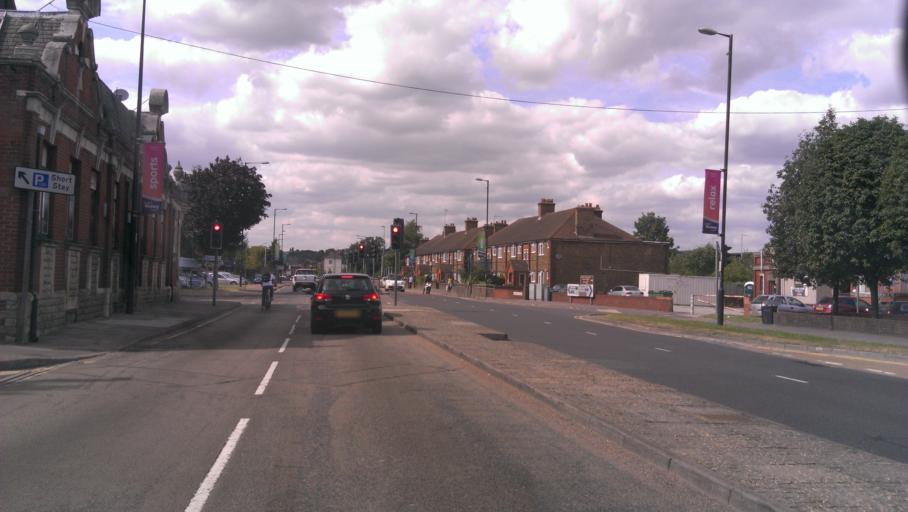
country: GB
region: England
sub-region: Medway
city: Rochester
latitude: 51.3876
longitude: 0.5072
